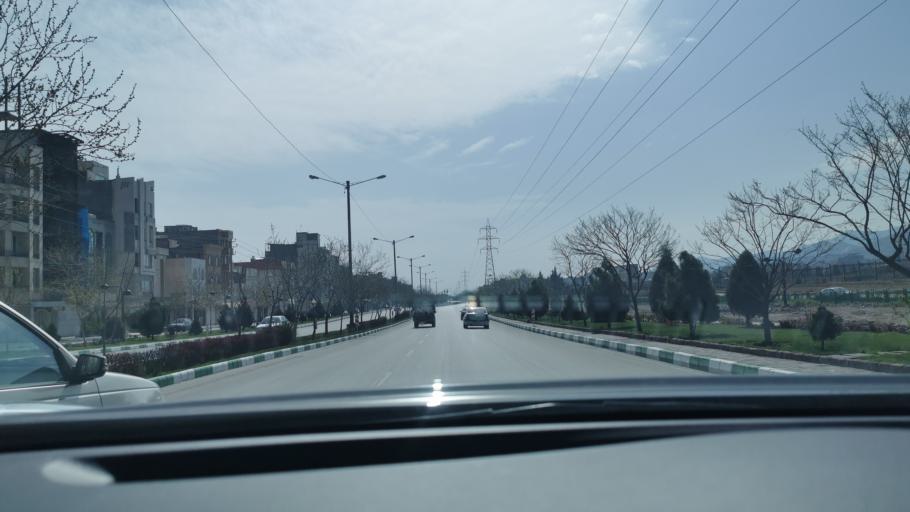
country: IR
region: Razavi Khorasan
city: Mashhad
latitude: 36.2865
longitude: 59.5377
